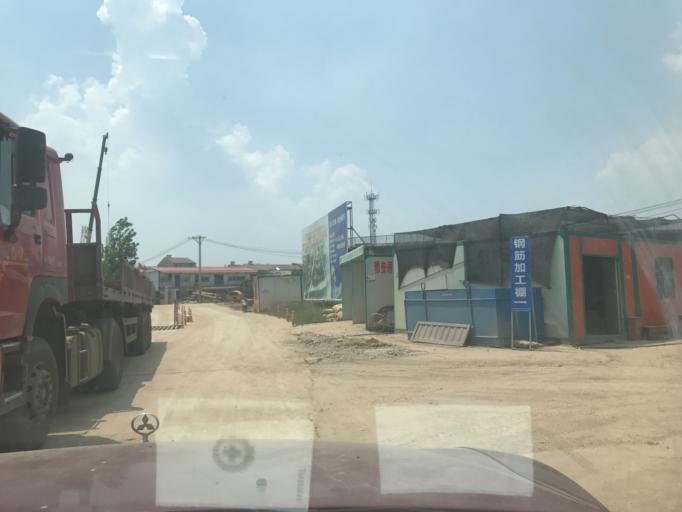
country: CN
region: Hubei
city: Shekou
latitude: 30.6912
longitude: 114.3393
